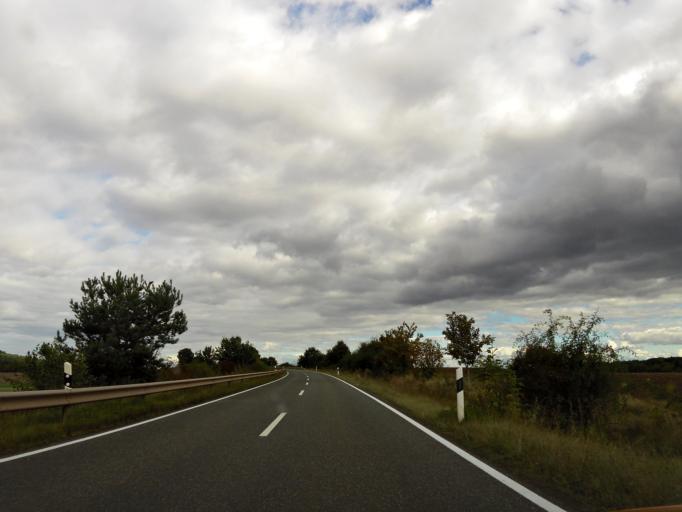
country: DE
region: Rheinland-Pfalz
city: Bennhausen
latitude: 49.6424
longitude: 7.9779
